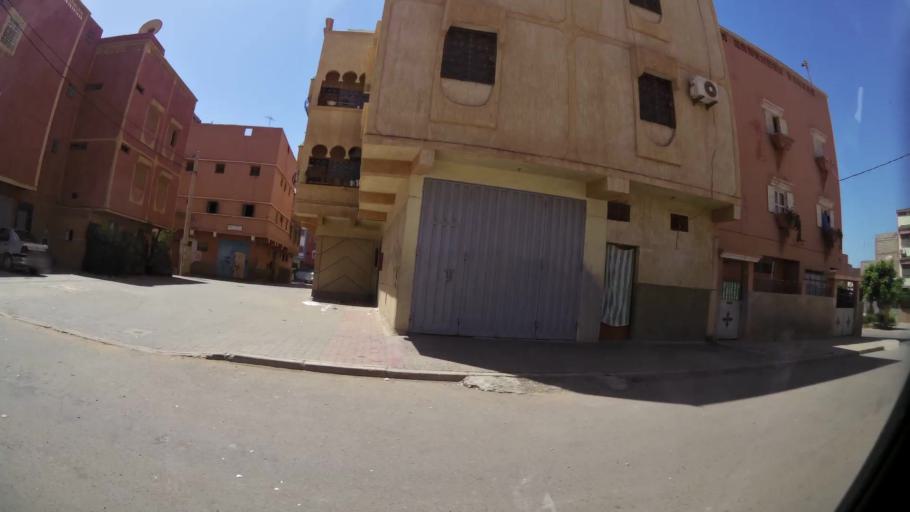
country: MA
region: Souss-Massa-Draa
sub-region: Inezgane-Ait Mellou
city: Inezgane
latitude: 30.3457
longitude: -9.4855
